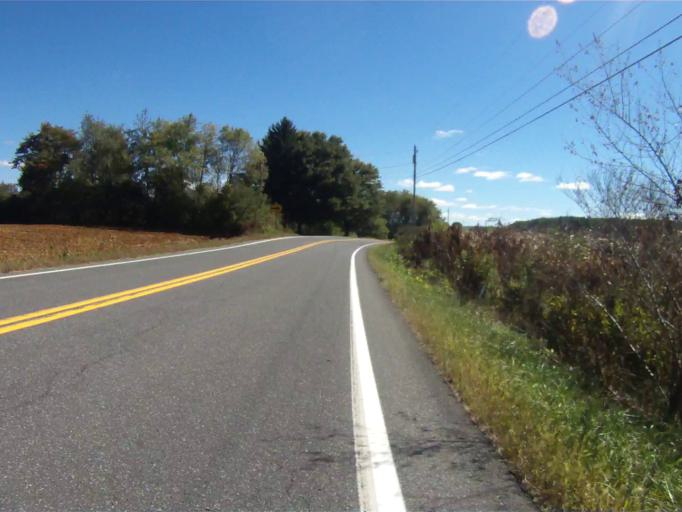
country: US
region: Pennsylvania
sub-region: Centre County
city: Houserville
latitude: 40.8436
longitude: -77.8756
